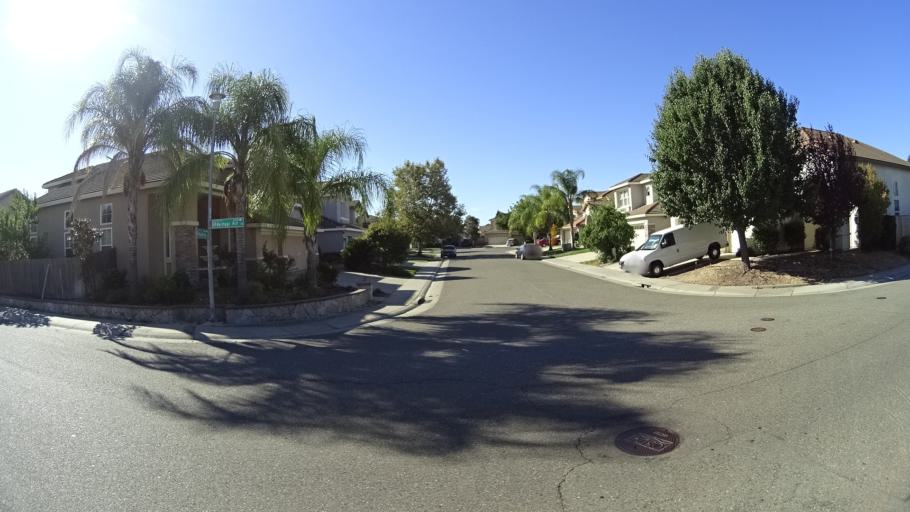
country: US
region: California
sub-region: Sacramento County
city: Vineyard
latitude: 38.4453
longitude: -121.3700
